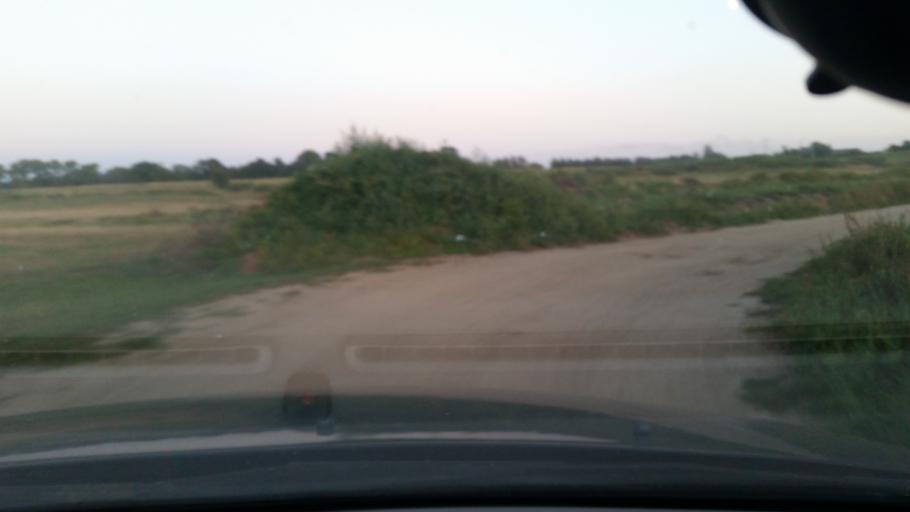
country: PL
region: Pomeranian Voivodeship
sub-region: Powiat wejherowski
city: Choczewo
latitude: 54.7756
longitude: 17.7943
